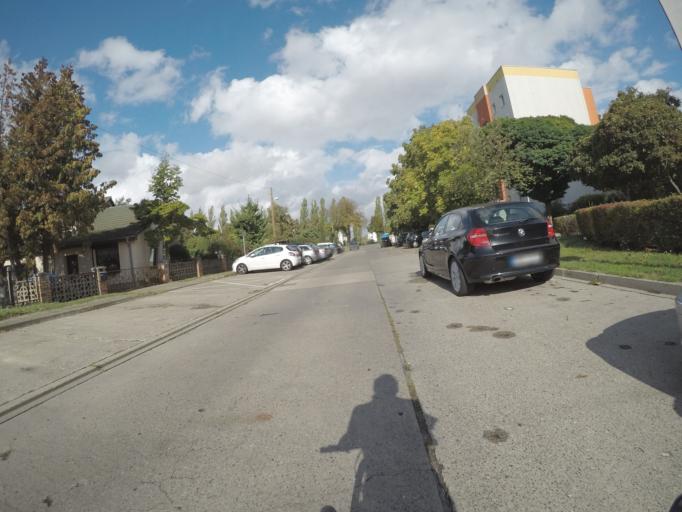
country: DE
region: Berlin
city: Falkenberg
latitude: 52.5705
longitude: 13.5608
